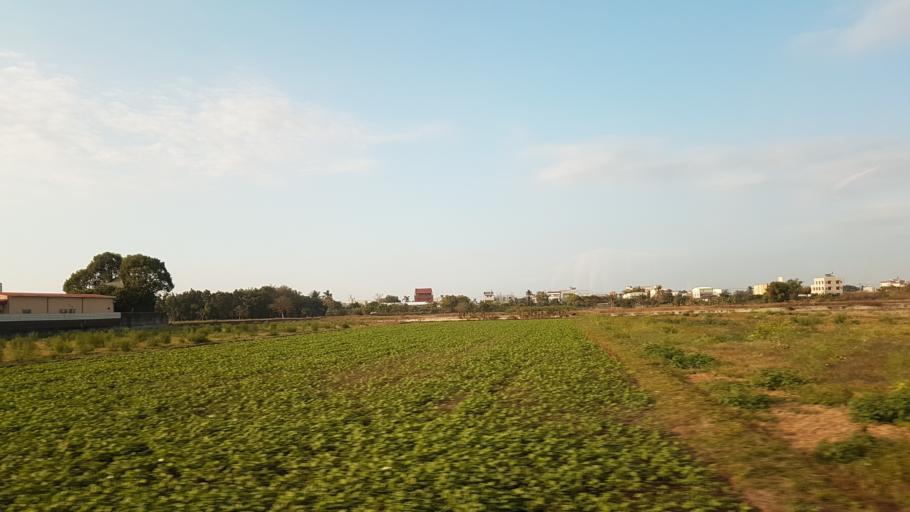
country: TW
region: Taiwan
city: Xinying
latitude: 23.3464
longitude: 120.3598
